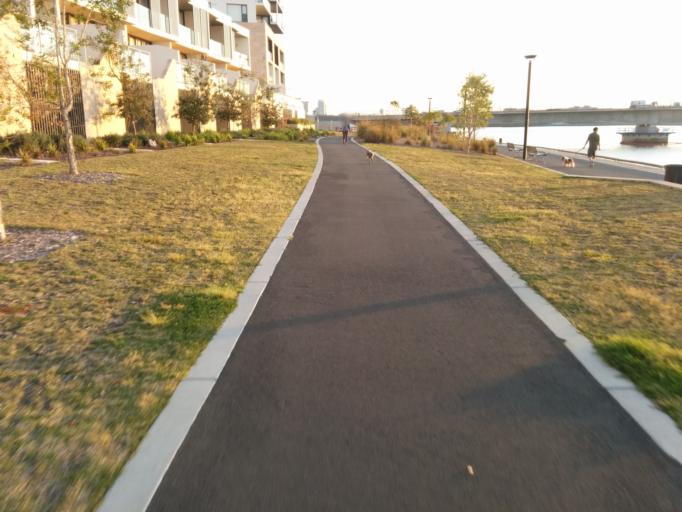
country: AU
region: New South Wales
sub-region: Canada Bay
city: Rhodes
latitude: -33.8271
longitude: 151.0839
